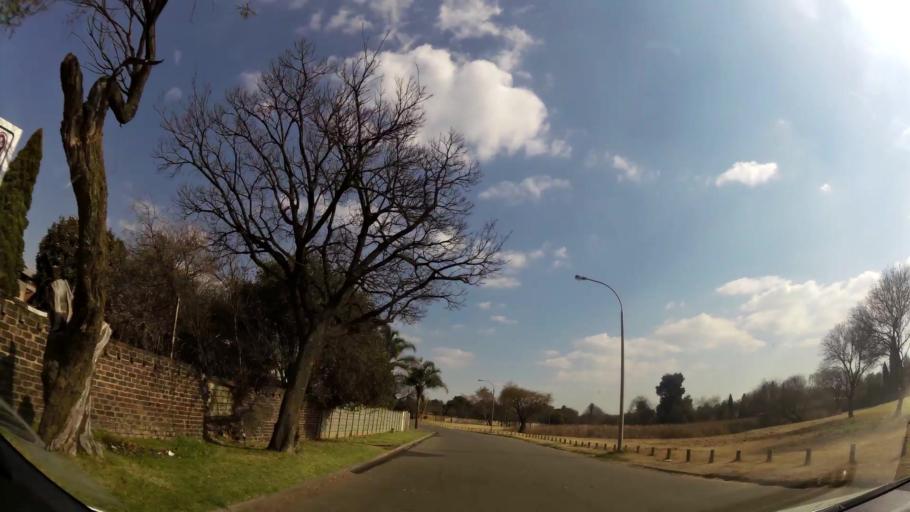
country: ZA
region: Gauteng
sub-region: Ekurhuleni Metropolitan Municipality
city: Germiston
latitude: -26.1937
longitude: 28.2040
